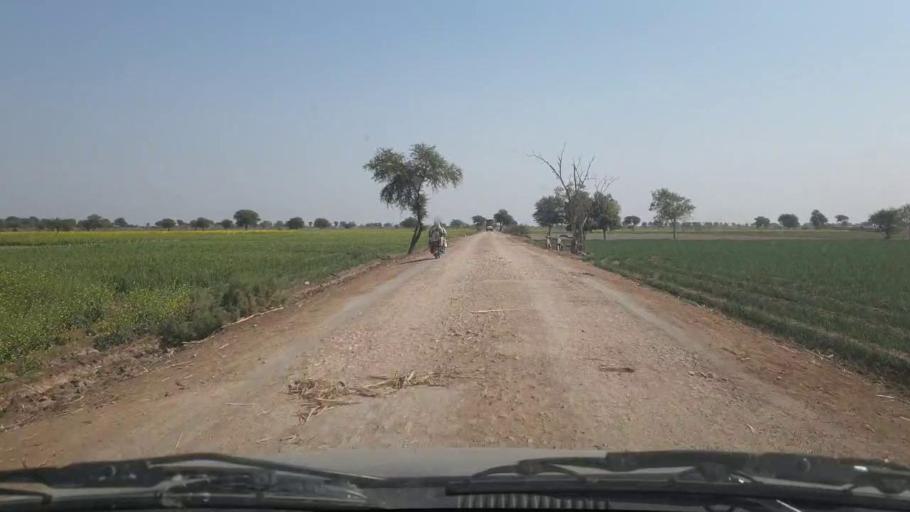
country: PK
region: Sindh
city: Samaro
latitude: 25.2441
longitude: 69.3659
